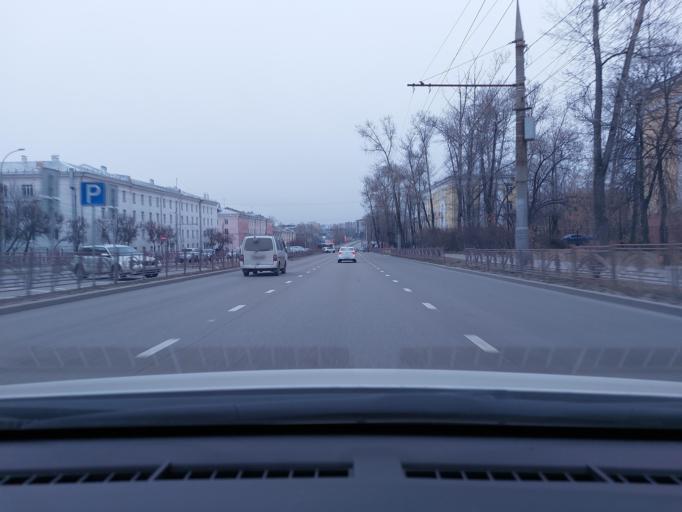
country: RU
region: Irkutsk
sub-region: Irkutskiy Rayon
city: Irkutsk
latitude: 52.2596
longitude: 104.2614
